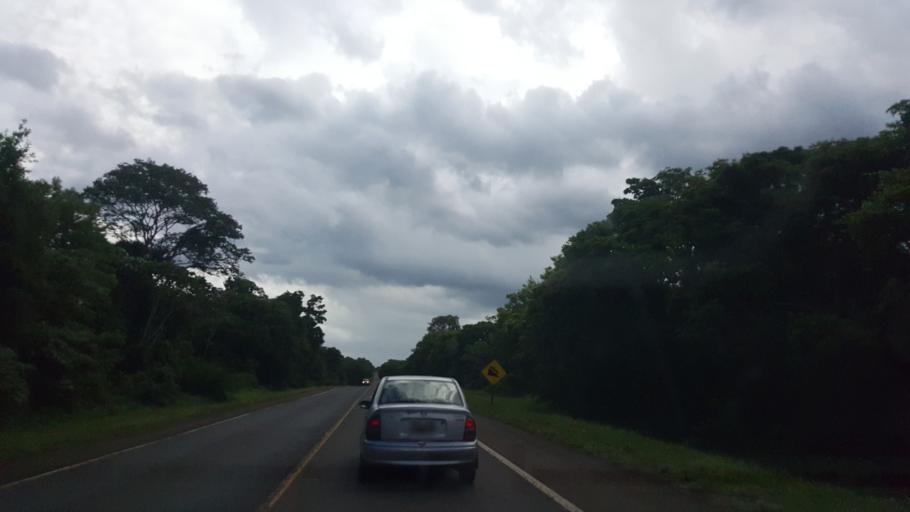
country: AR
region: Misiones
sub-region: Departamento de Iguazu
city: Puerto Iguazu
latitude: -25.7197
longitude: -54.5224
